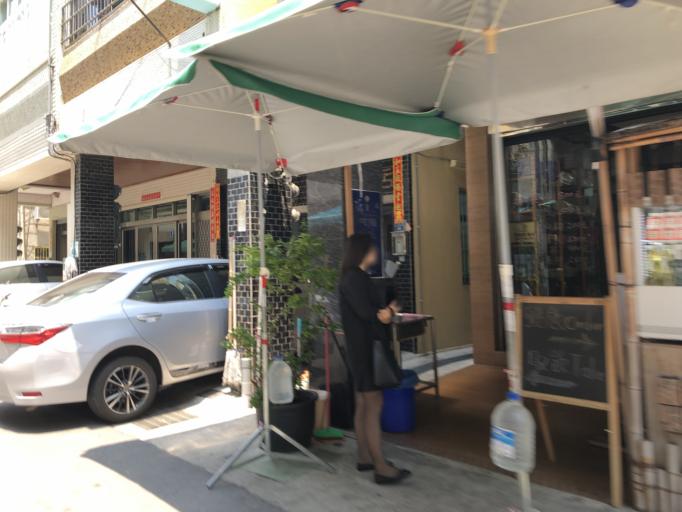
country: TW
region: Kaohsiung
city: Kaohsiung
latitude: 22.6214
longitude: 120.2726
